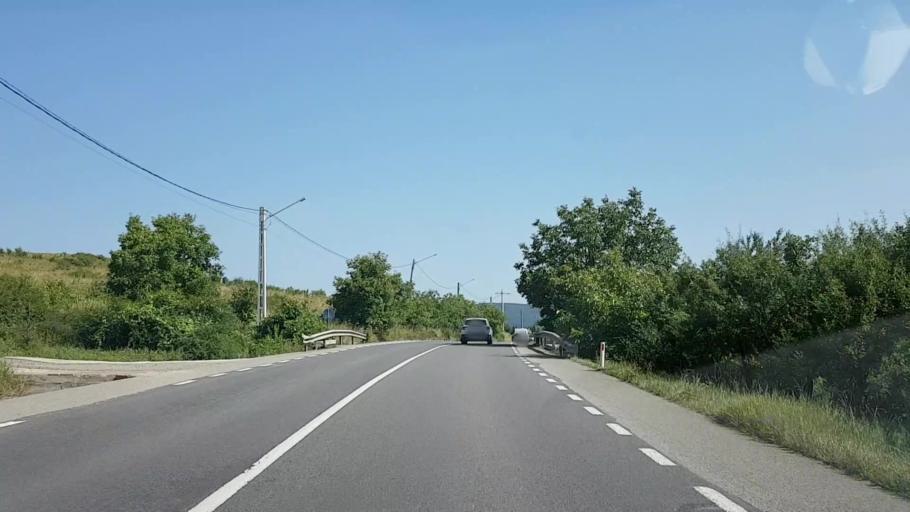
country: RO
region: Bistrita-Nasaud
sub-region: Comuna Sieu-Magherus
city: Sieu-Magherus
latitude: 47.0772
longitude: 24.3972
